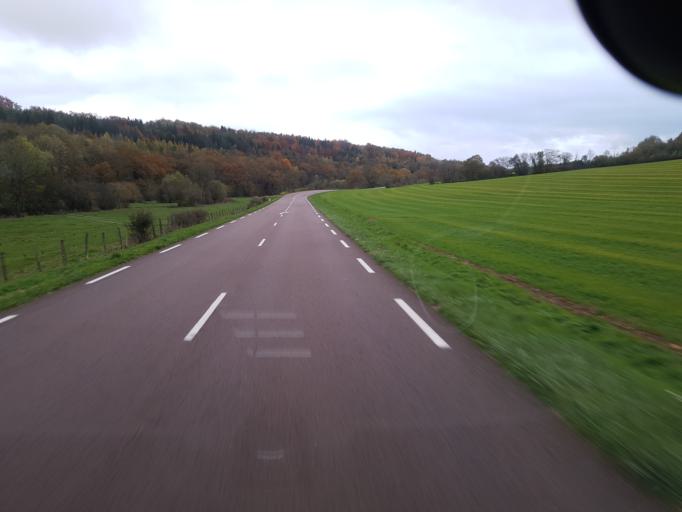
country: FR
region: Bourgogne
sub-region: Departement de la Cote-d'Or
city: Chatillon-sur-Seine
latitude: 47.6790
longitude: 4.6986
